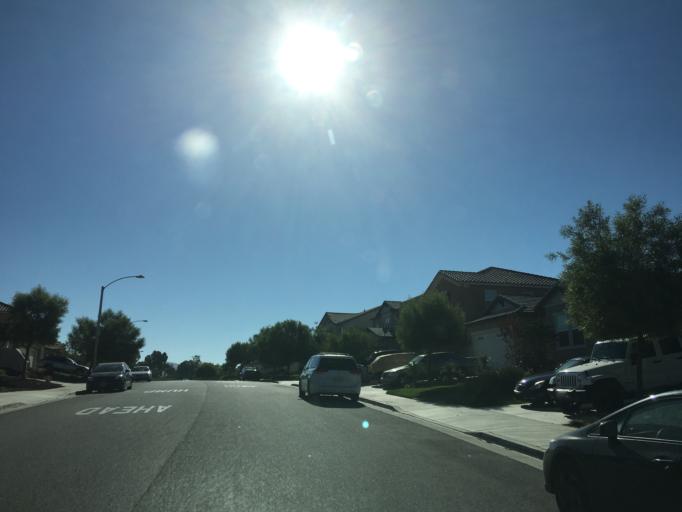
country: US
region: California
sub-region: Los Angeles County
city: Santa Clarita
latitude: 34.4385
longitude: -118.4913
